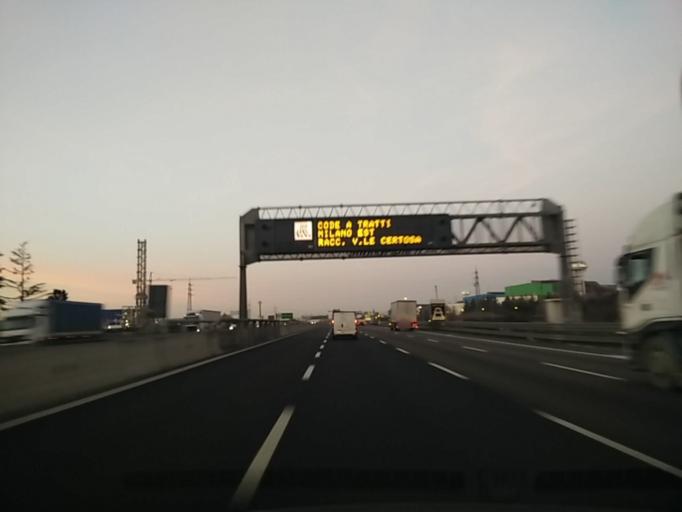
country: IT
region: Lombardy
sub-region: Provincia di Bergamo
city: Dalmine
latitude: 45.6399
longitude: 9.6128
